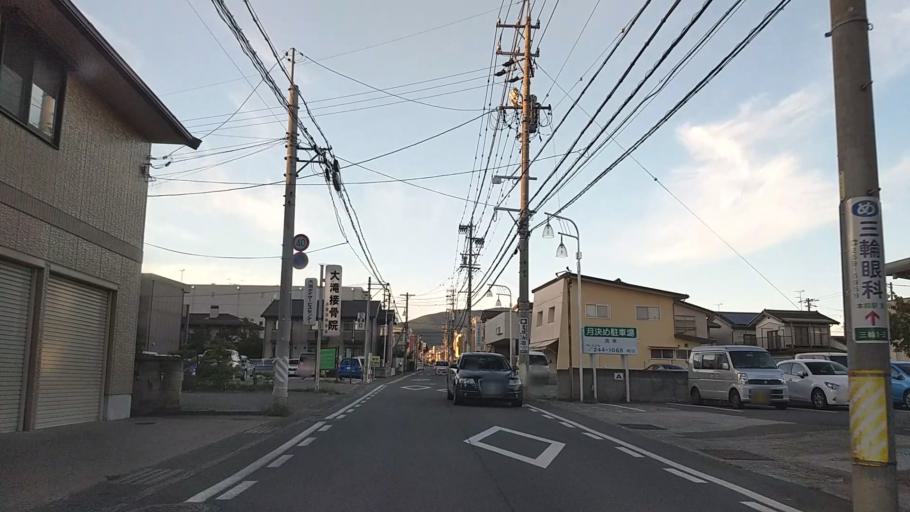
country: JP
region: Nagano
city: Nagano-shi
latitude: 36.6560
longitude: 138.2033
